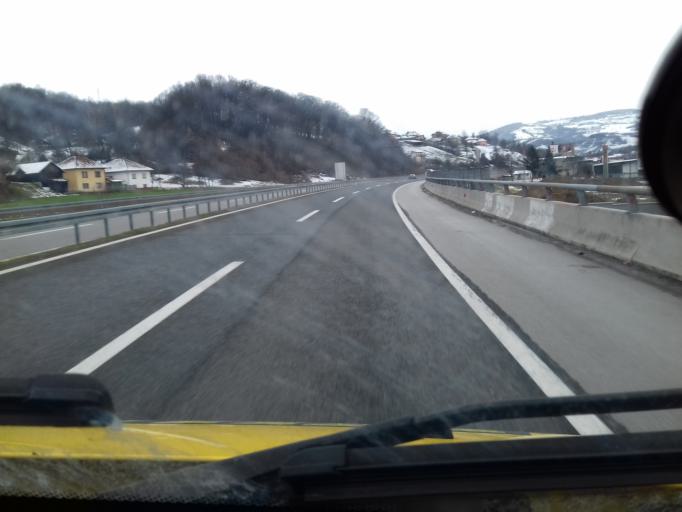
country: BA
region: Federation of Bosnia and Herzegovina
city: Visoko
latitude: 44.0039
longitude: 18.1760
